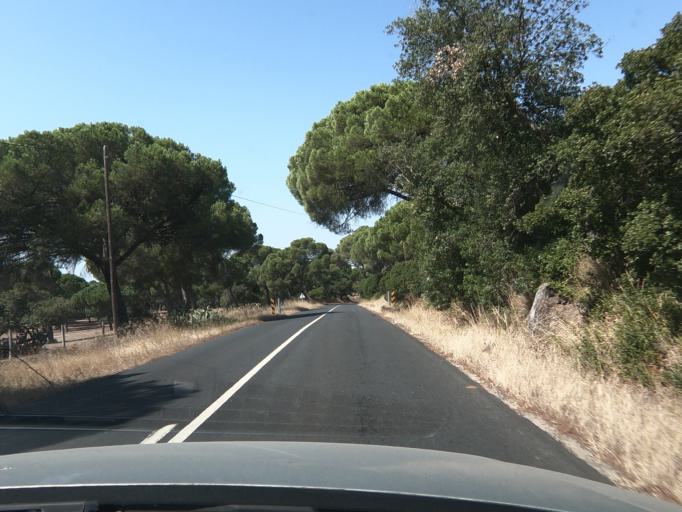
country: PT
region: Setubal
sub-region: Alcacer do Sal
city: Alcacer do Sal
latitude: 38.3515
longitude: -8.4679
